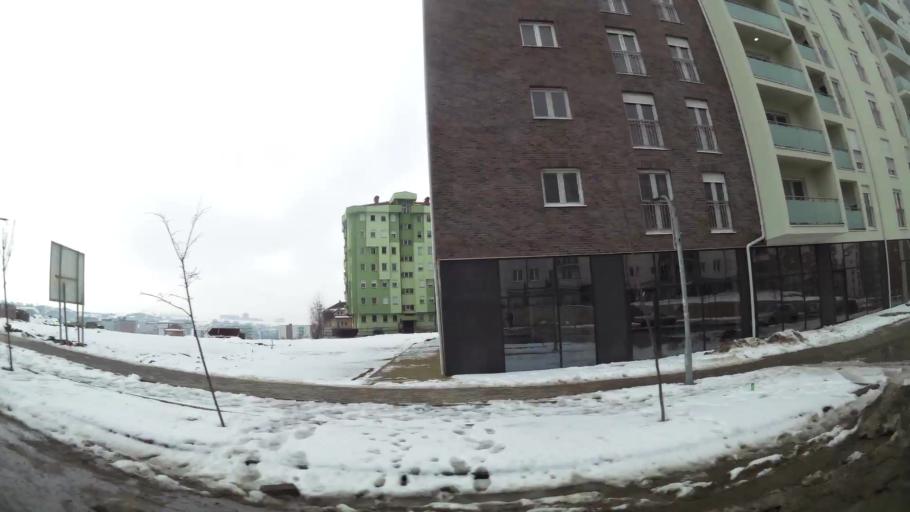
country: XK
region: Pristina
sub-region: Komuna e Prishtines
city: Pristina
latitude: 42.6504
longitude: 21.1783
